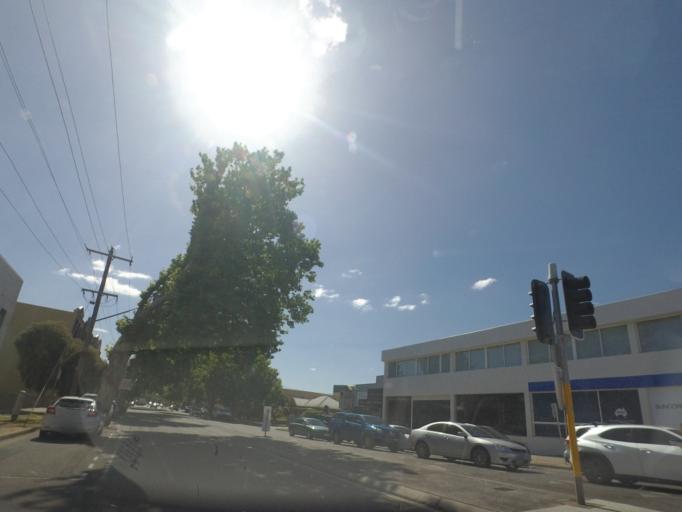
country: AU
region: New South Wales
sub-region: Albury Municipality
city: South Albury
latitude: -36.0828
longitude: 146.9151
